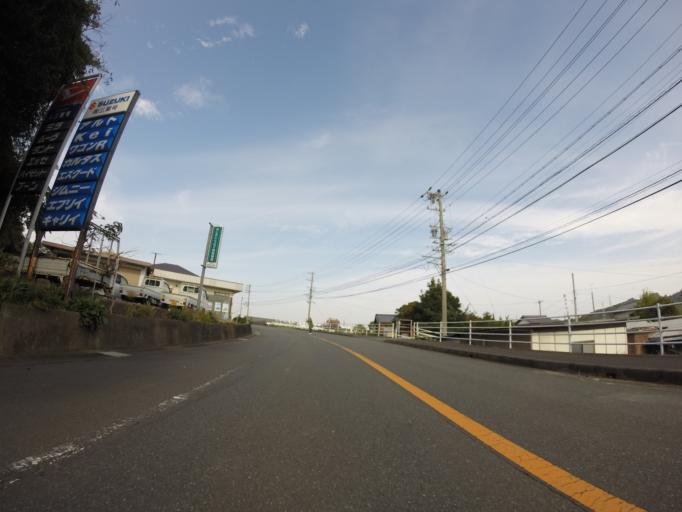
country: JP
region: Shizuoka
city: Shimada
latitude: 34.7582
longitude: 138.1959
